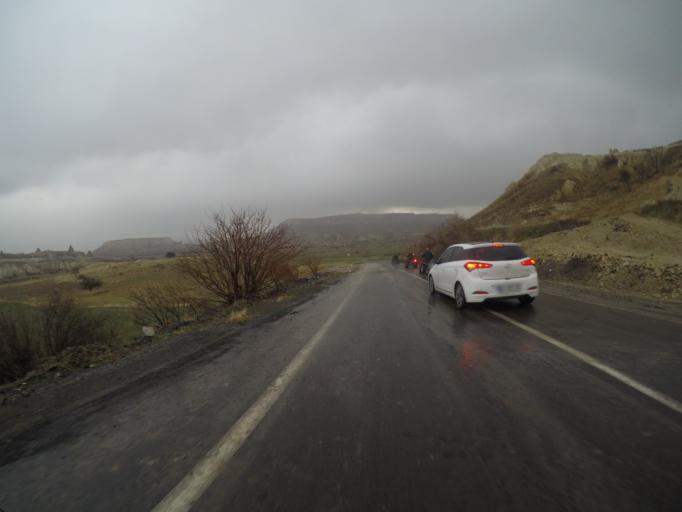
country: TR
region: Nevsehir
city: Goereme
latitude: 38.6670
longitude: 34.8224
